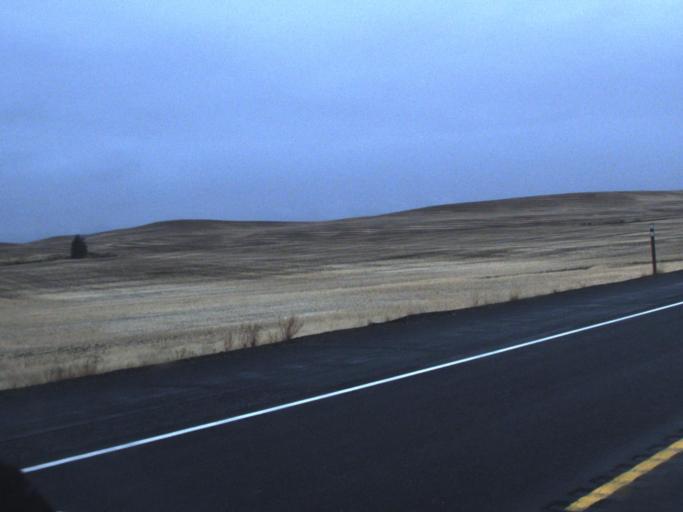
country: US
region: Washington
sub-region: Spokane County
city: Cheney
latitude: 47.4159
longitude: -117.3916
